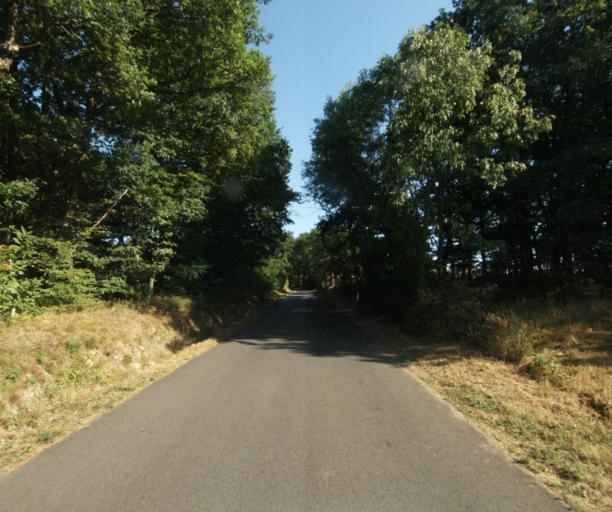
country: FR
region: Rhone-Alpes
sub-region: Departement du Rhone
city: Sainte-Consorce
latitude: 45.8017
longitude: 4.6913
